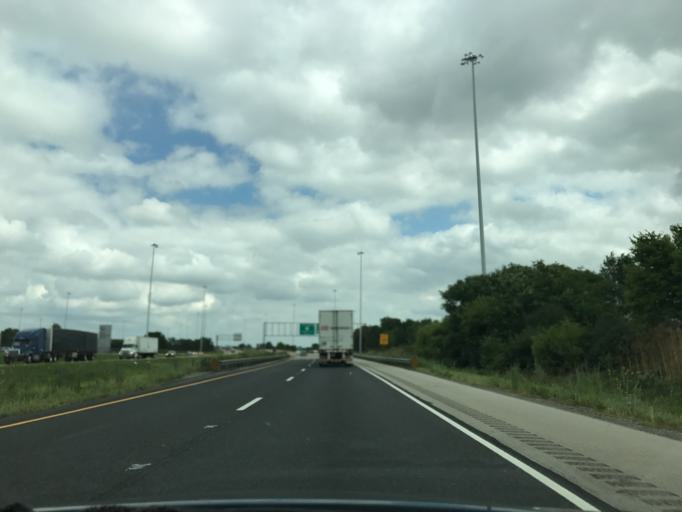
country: US
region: Illinois
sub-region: Will County
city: Shorewood
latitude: 41.4882
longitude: -88.1734
